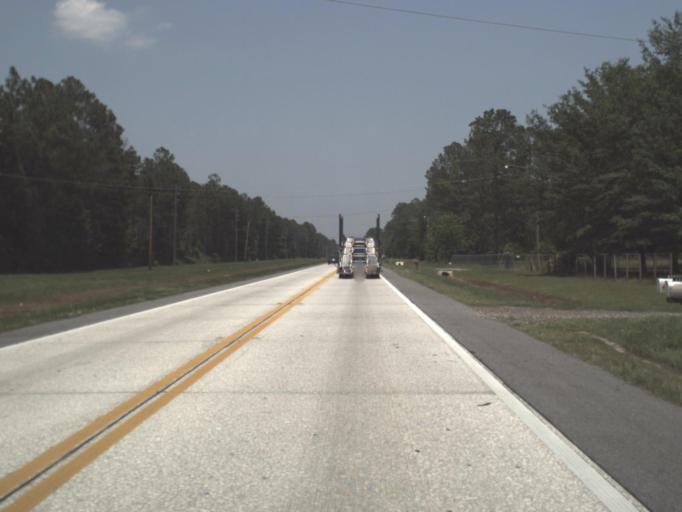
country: US
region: Florida
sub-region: Duval County
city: Baldwin
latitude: 30.2336
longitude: -81.9135
